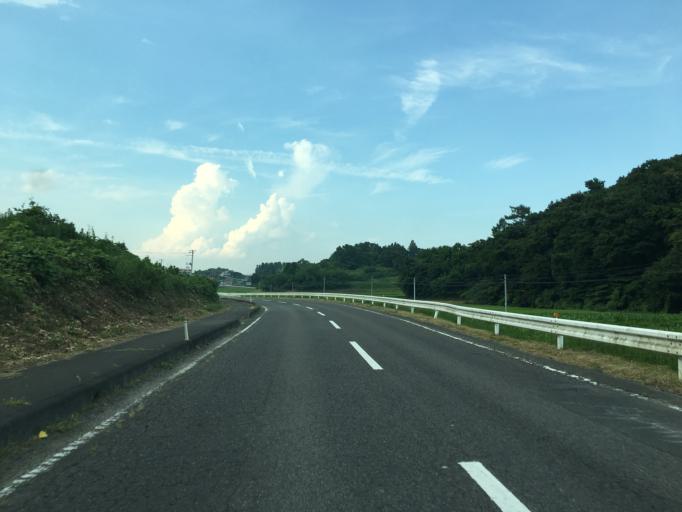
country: JP
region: Fukushima
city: Motomiya
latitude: 37.5185
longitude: 140.4442
